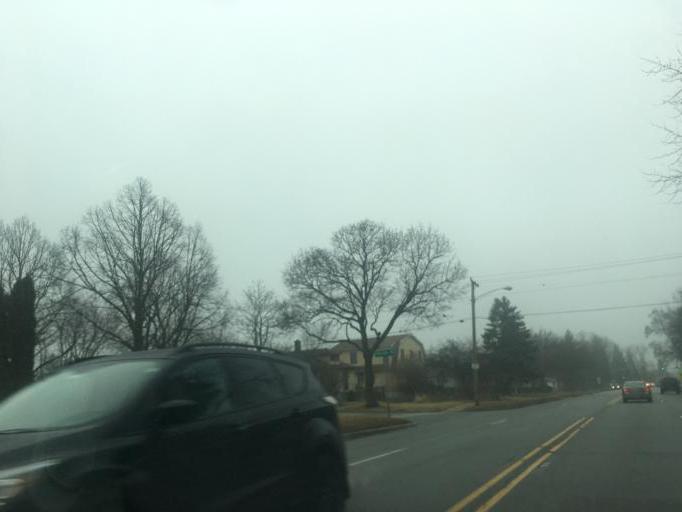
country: US
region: Illinois
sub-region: DuPage County
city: Downers Grove
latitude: 41.8018
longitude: -88.0376
